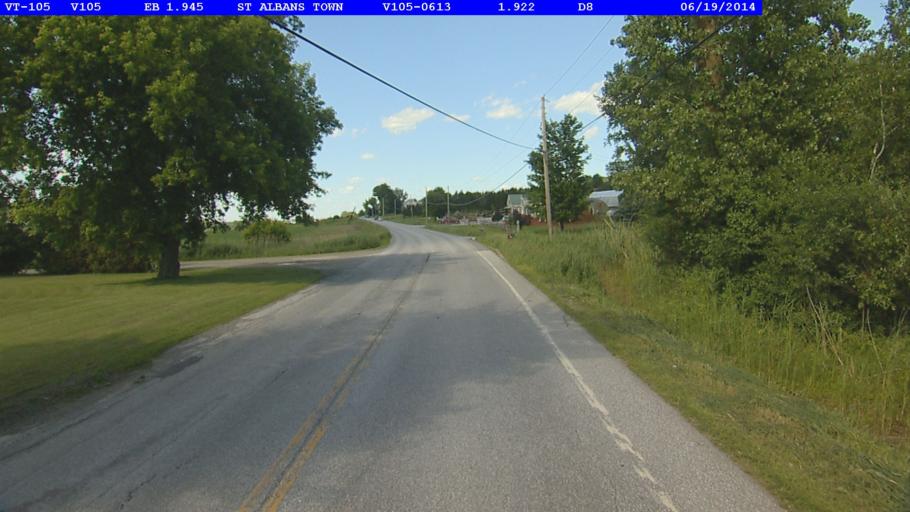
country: US
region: Vermont
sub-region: Franklin County
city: Saint Albans
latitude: 44.8345
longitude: -73.0479
